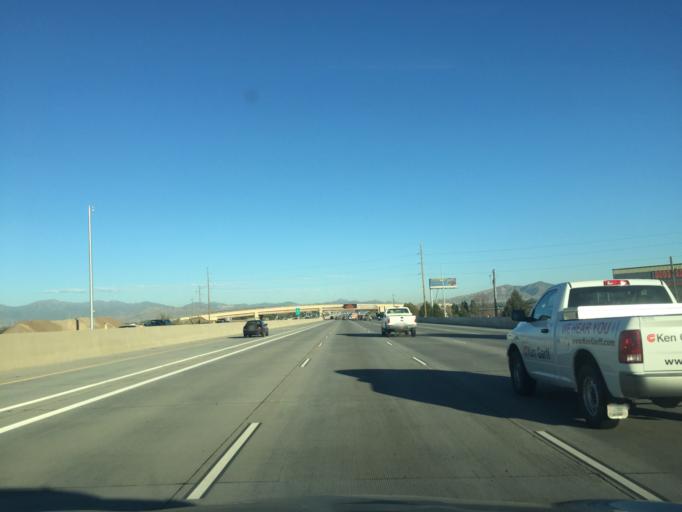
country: US
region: Utah
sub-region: Utah County
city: Pleasant Grove
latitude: 40.3425
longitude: -111.7571
